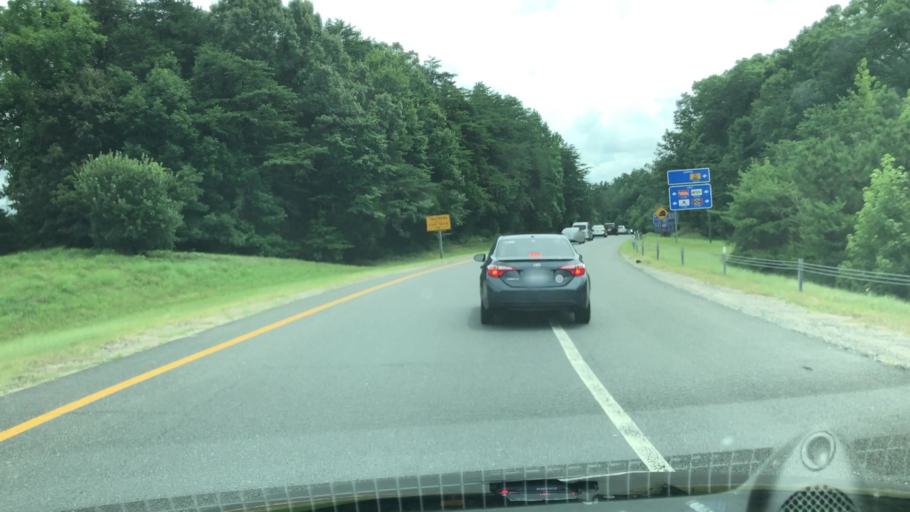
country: US
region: Virginia
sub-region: City of Fredericksburg
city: Fredericksburg
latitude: 38.2409
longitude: -77.5013
